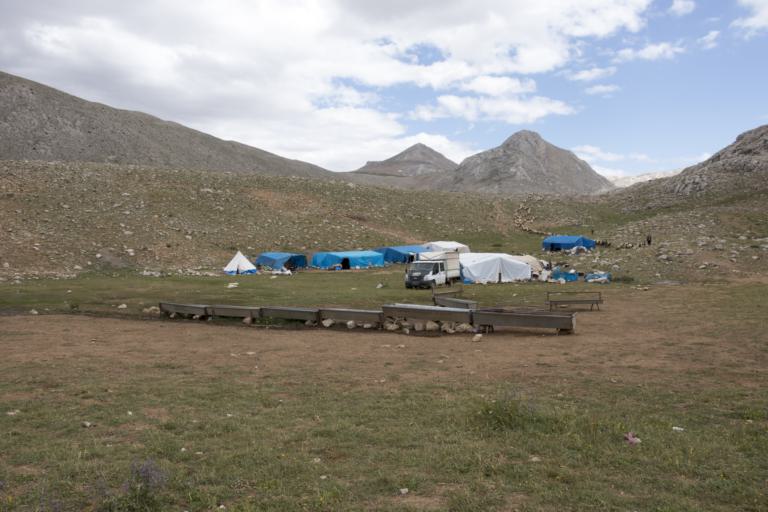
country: TR
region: Adana
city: Tufanbeyli
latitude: 38.4204
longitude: 36.1905
